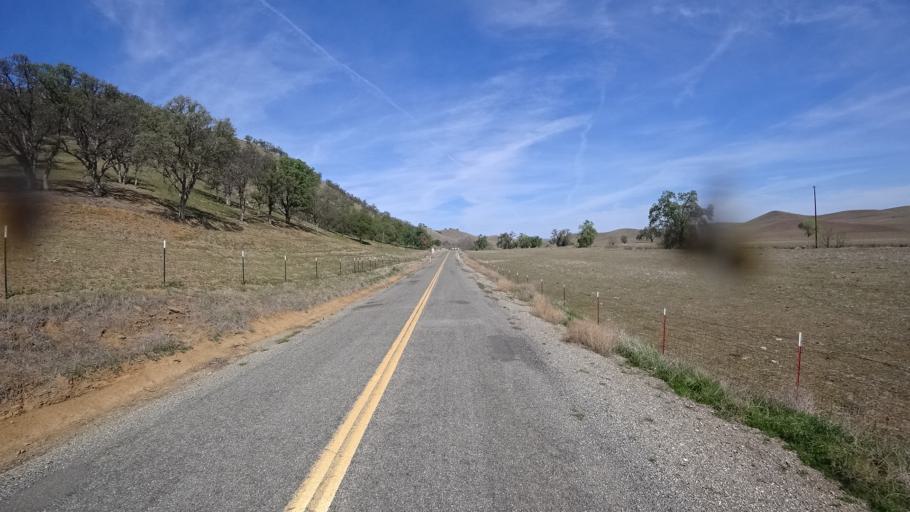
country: US
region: California
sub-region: Glenn County
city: Willows
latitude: 39.5425
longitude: -122.3970
